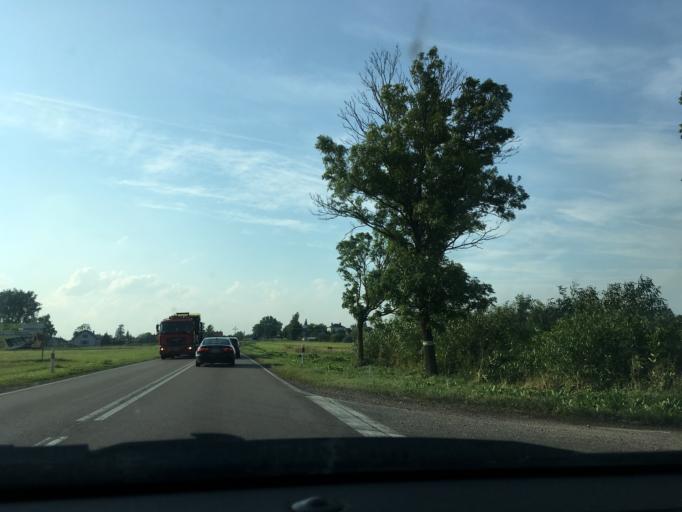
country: PL
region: Podlasie
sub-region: Powiat moniecki
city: Knyszyn
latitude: 53.3058
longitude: 22.9174
